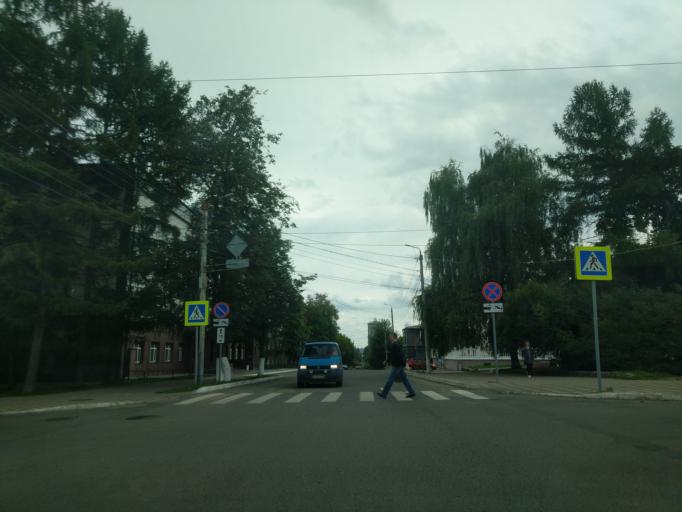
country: RU
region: Kirov
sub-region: Kirovo-Chepetskiy Rayon
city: Kirov
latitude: 58.6037
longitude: 49.6720
